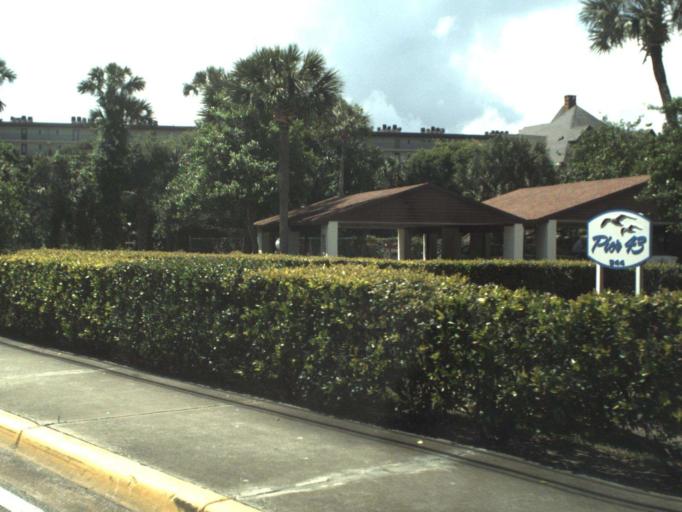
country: US
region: Florida
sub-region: Volusia County
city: Daytona Beach
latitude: 29.2136
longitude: -81.0069
